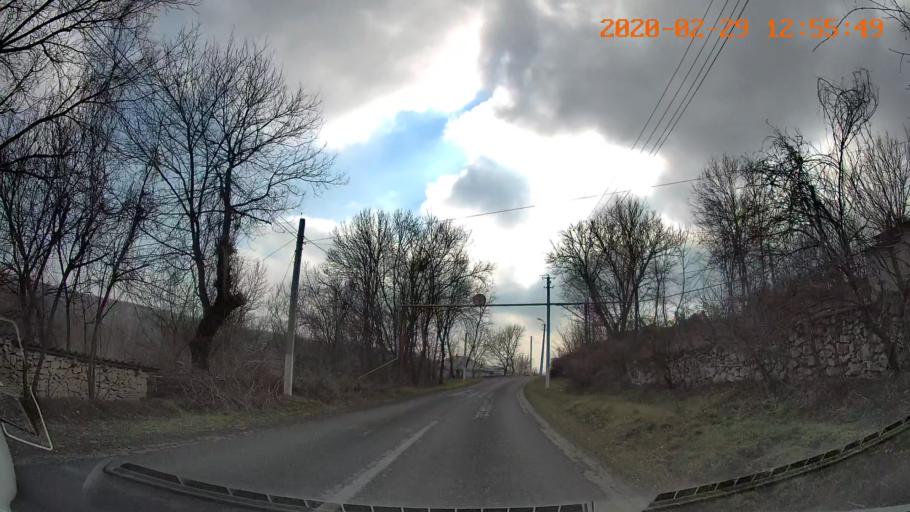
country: MD
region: Telenesti
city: Camenca
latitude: 48.0917
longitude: 28.7244
